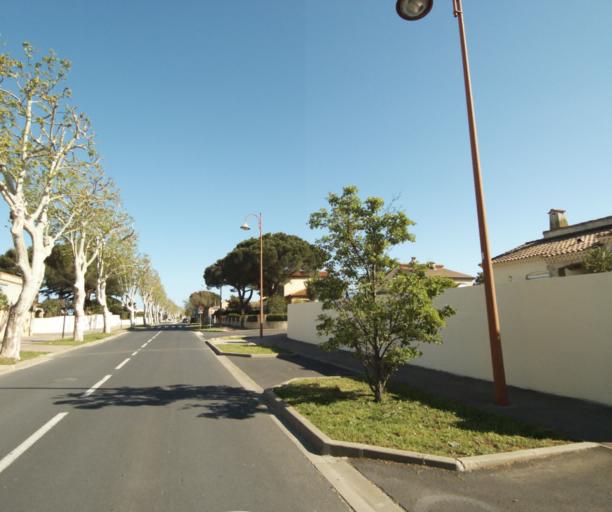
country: FR
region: Languedoc-Roussillon
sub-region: Departement de l'Herault
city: Perols
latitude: 43.5684
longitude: 3.9463
